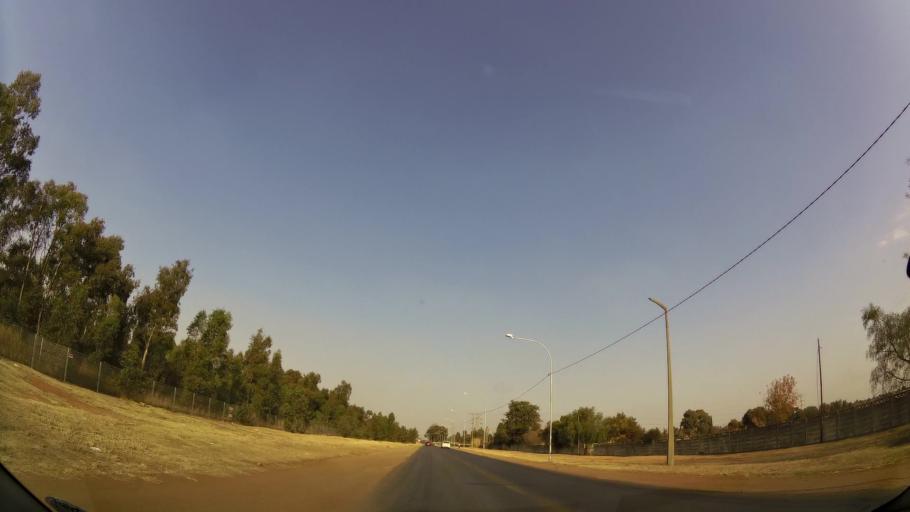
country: ZA
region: Gauteng
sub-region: Ekurhuleni Metropolitan Municipality
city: Benoni
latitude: -26.1116
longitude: 28.3717
